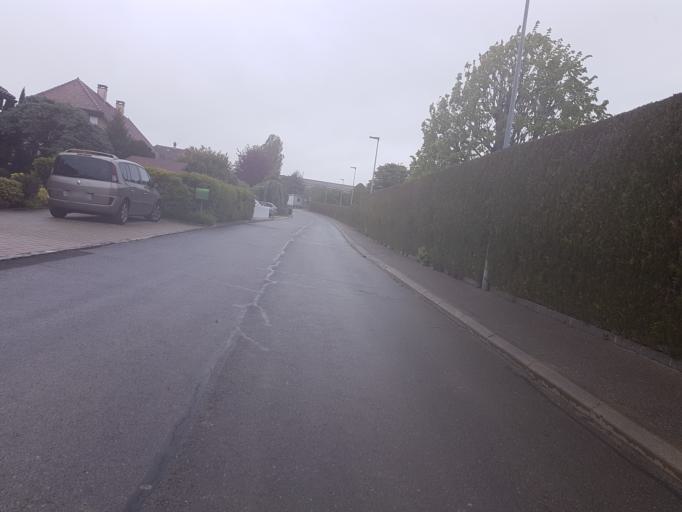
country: CH
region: Vaud
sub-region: Morges District
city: Preverenges
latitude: 46.5148
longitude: 6.5293
